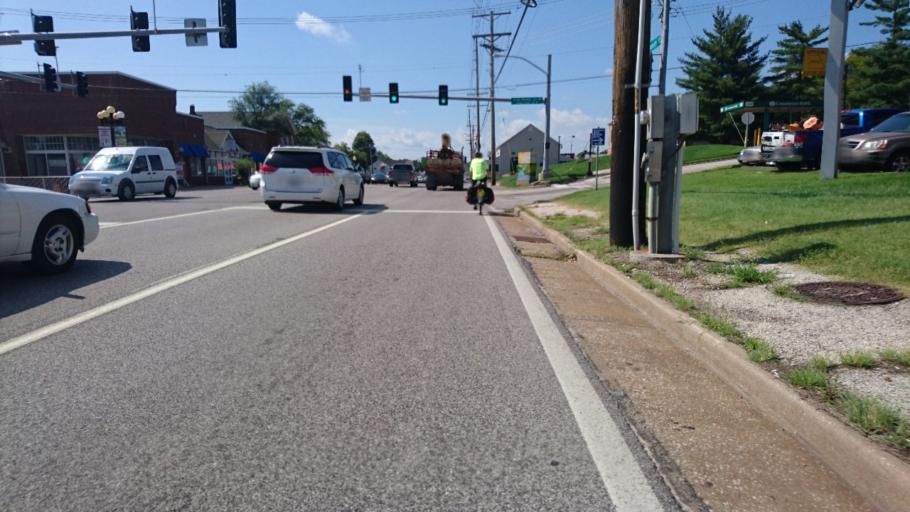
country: US
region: Missouri
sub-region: Saint Louis County
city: Manchester
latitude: 38.5930
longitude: -90.5113
